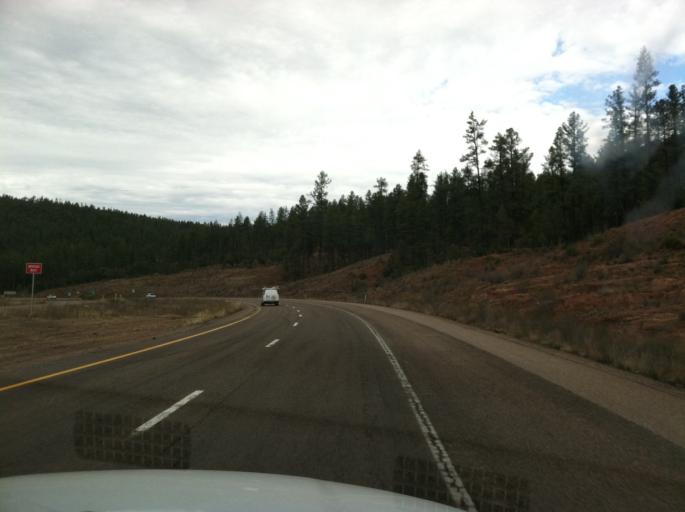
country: US
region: Arizona
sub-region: Gila County
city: Star Valley
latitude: 34.3283
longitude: -111.0884
